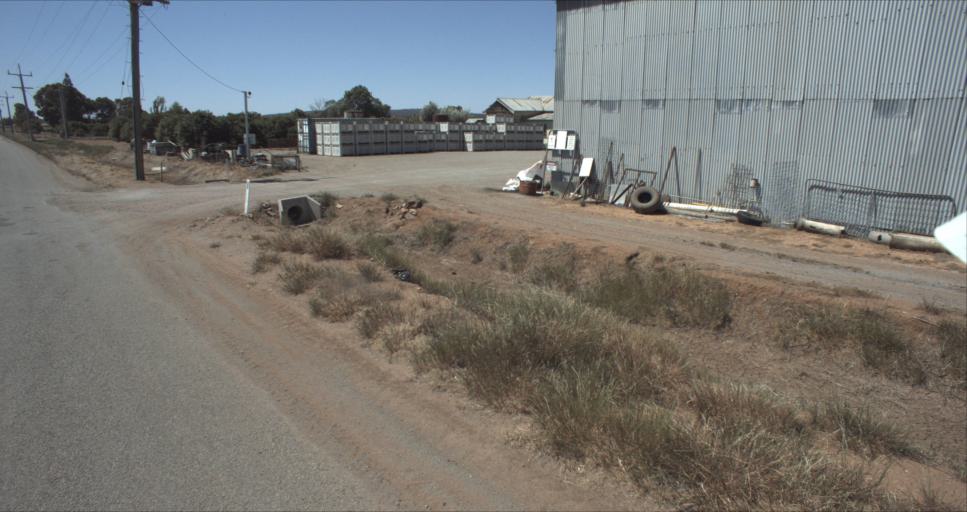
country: AU
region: New South Wales
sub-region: Leeton
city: Leeton
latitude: -34.4952
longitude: 146.4214
